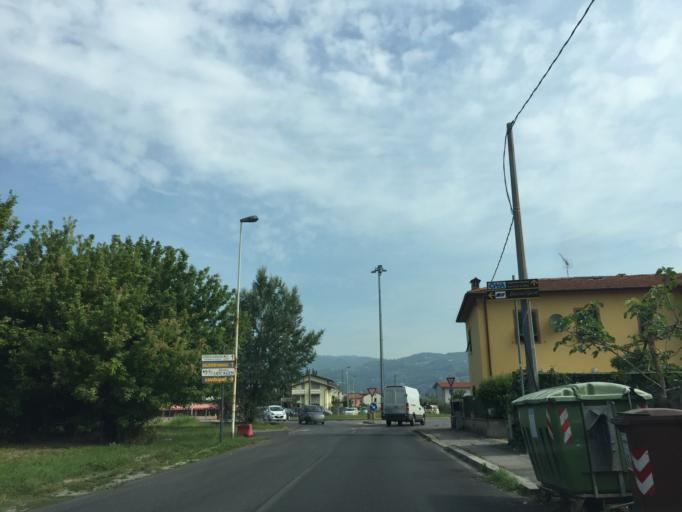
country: IT
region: Tuscany
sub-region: Provincia di Pistoia
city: Montecatini-Terme
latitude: 43.8678
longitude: 10.7671
